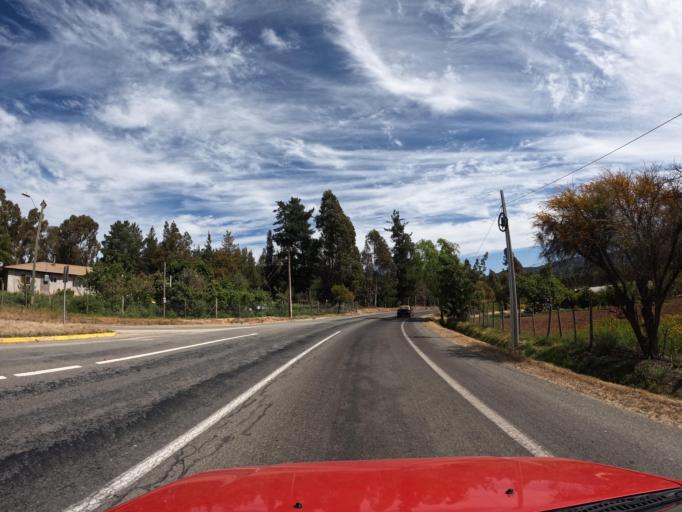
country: CL
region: Maule
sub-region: Provincia de Talca
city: Talca
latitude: -35.1290
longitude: -71.9554
